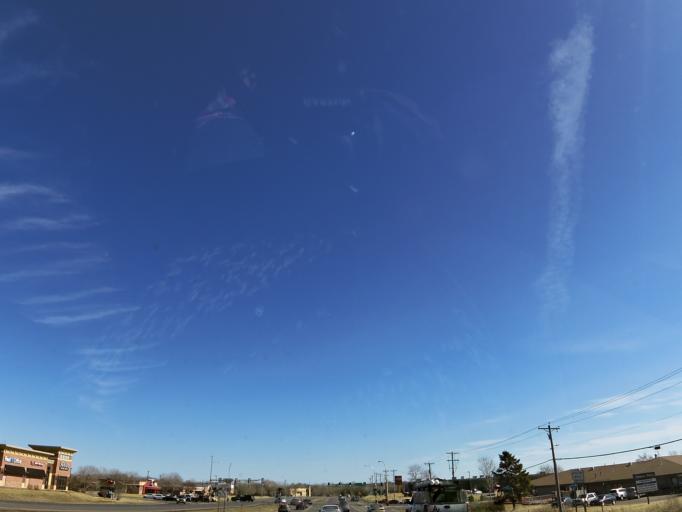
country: US
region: Minnesota
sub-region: Hennepin County
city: Plymouth
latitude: 45.0091
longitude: -93.4529
